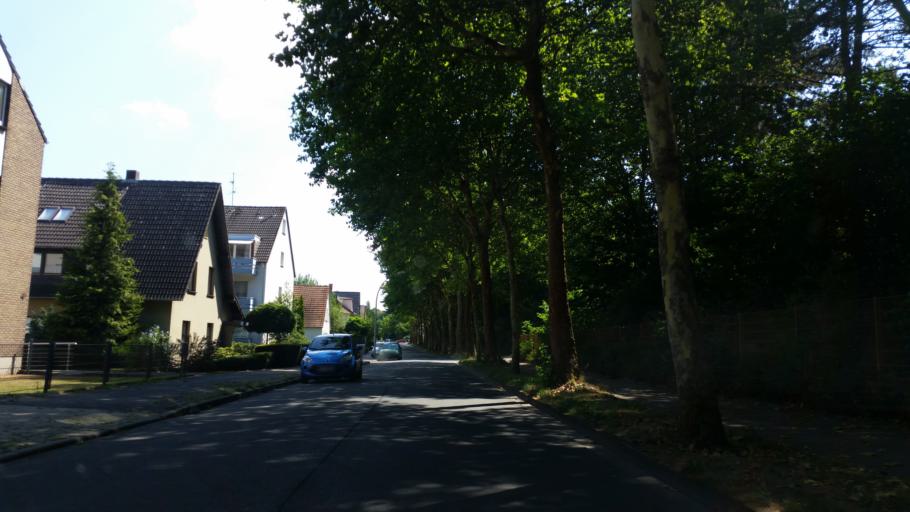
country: DE
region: North Rhine-Westphalia
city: Bad Oeynhausen
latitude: 52.2039
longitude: 8.8165
